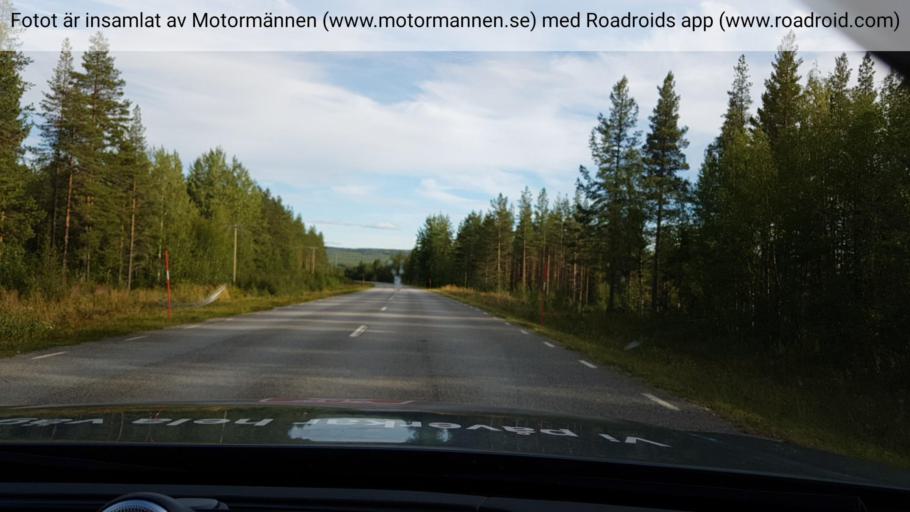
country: SE
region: Jaemtland
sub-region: Stroemsunds Kommun
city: Stroemsund
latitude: 64.2599
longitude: 15.3999
